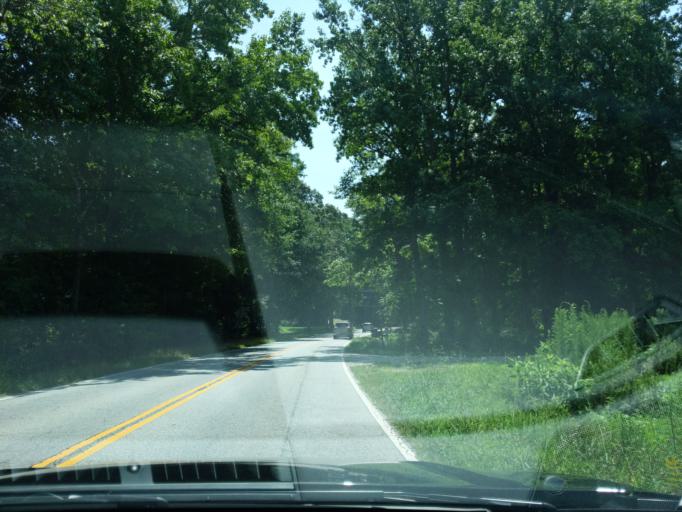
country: US
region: South Carolina
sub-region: Greenville County
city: Five Forks
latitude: 34.7676
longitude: -82.2062
